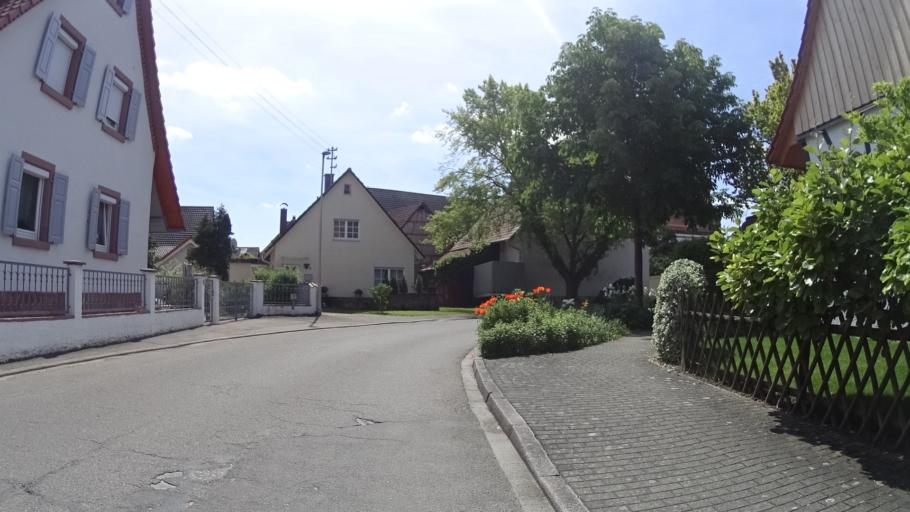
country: DE
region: Baden-Wuerttemberg
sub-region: Freiburg Region
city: Meissenheim
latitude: 48.4122
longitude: 7.7766
